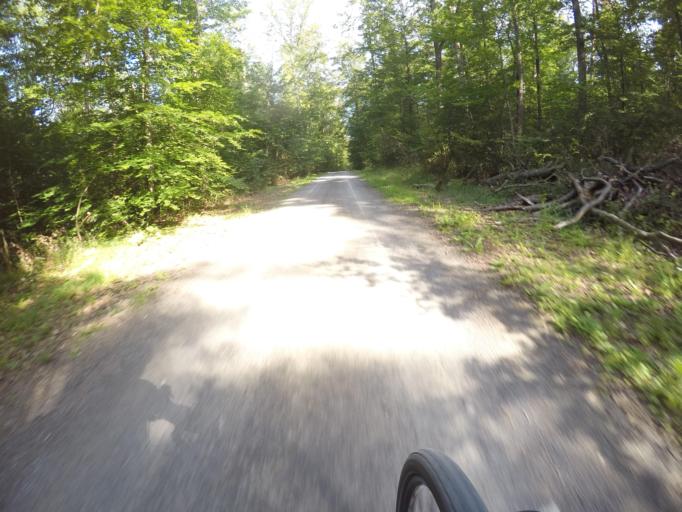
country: DE
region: Baden-Wuerttemberg
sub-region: Regierungsbezirk Stuttgart
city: Weissach
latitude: 48.8675
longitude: 8.9032
